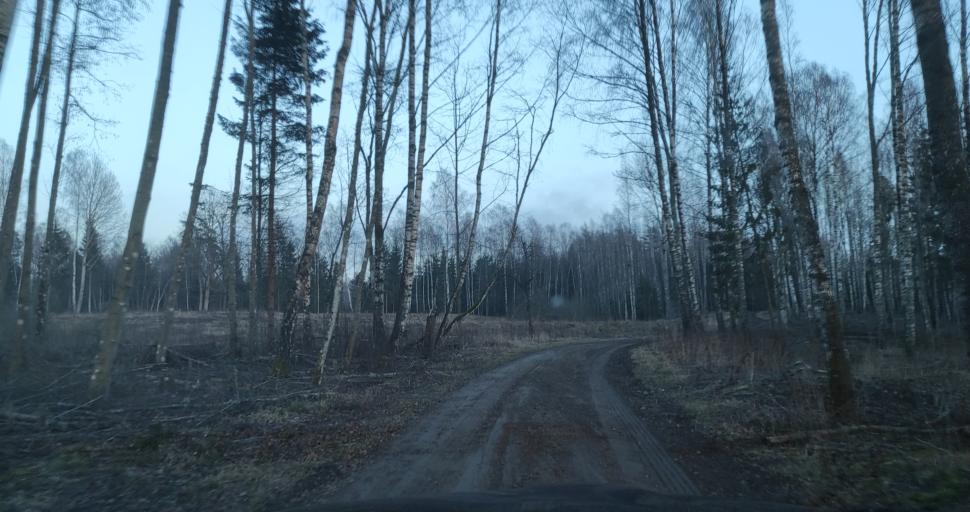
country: LV
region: Kuldigas Rajons
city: Kuldiga
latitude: 56.8120
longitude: 21.8259
